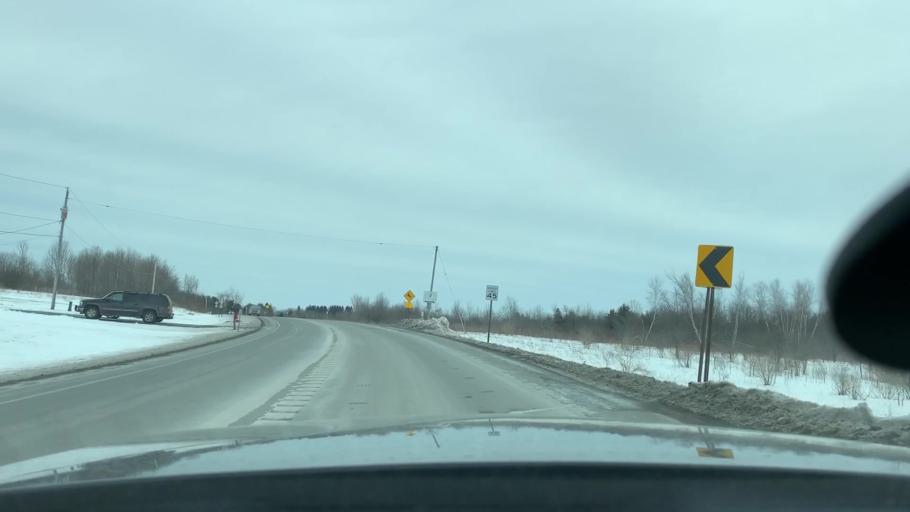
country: US
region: New York
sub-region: Oneida County
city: Utica
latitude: 43.0334
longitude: -75.1838
